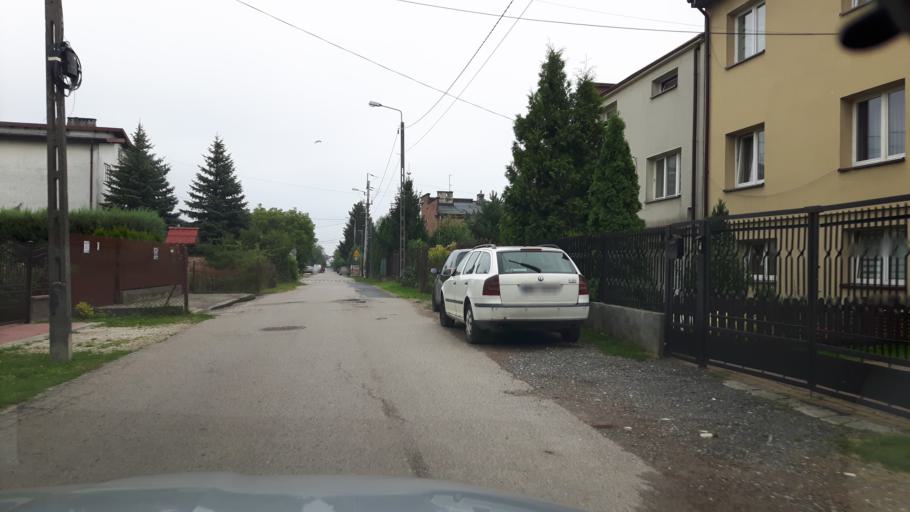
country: PL
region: Masovian Voivodeship
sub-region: Powiat wolominski
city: Marki
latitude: 52.3207
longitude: 21.1082
